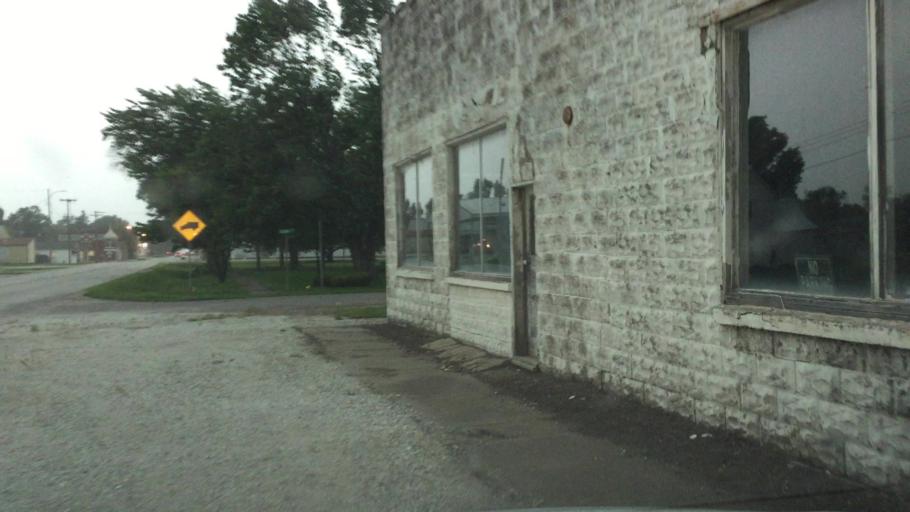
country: US
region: Illinois
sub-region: Adams County
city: Camp Point
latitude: 40.2317
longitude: -91.0603
